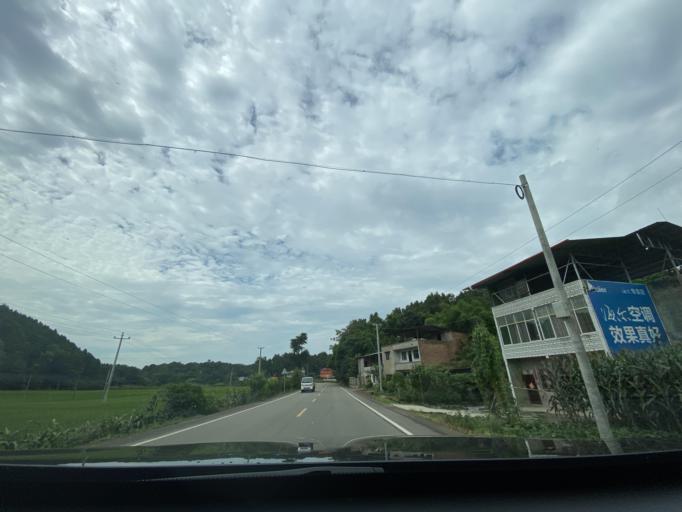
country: CN
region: Sichuan
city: Jiancheng
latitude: 30.4725
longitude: 104.6298
